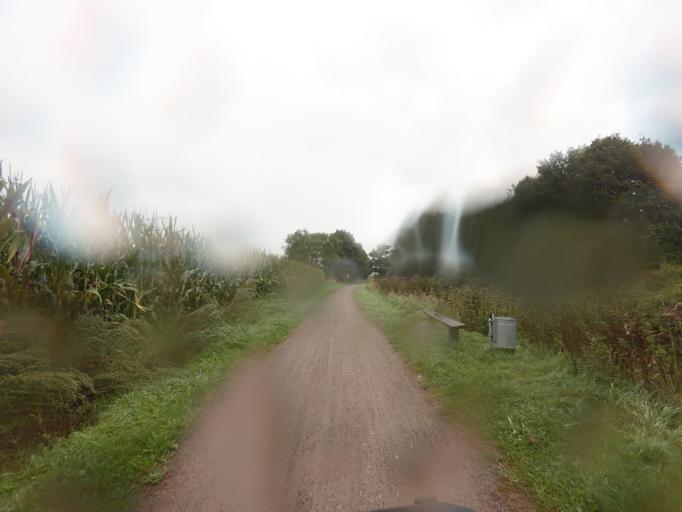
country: DE
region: North Rhine-Westphalia
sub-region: Regierungsbezirk Munster
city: Gronau
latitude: 52.1934
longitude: 7.0177
